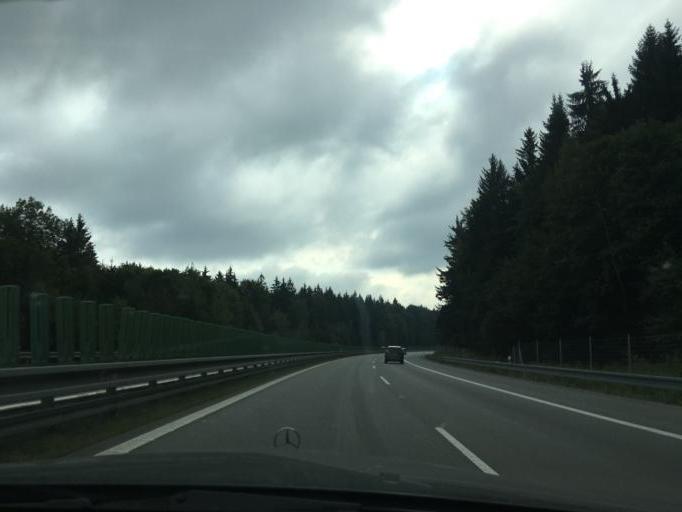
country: CZ
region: Vysocina
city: Stoky
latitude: 49.4784
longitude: 15.5581
